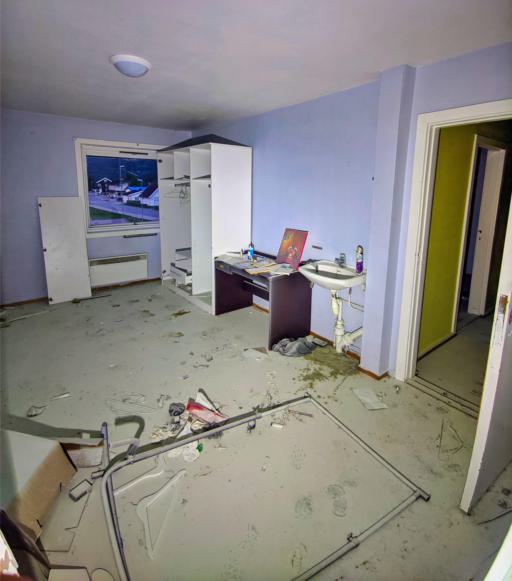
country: NO
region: Buskerud
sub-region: Gol
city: Gol
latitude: 60.7017
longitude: 8.9602
